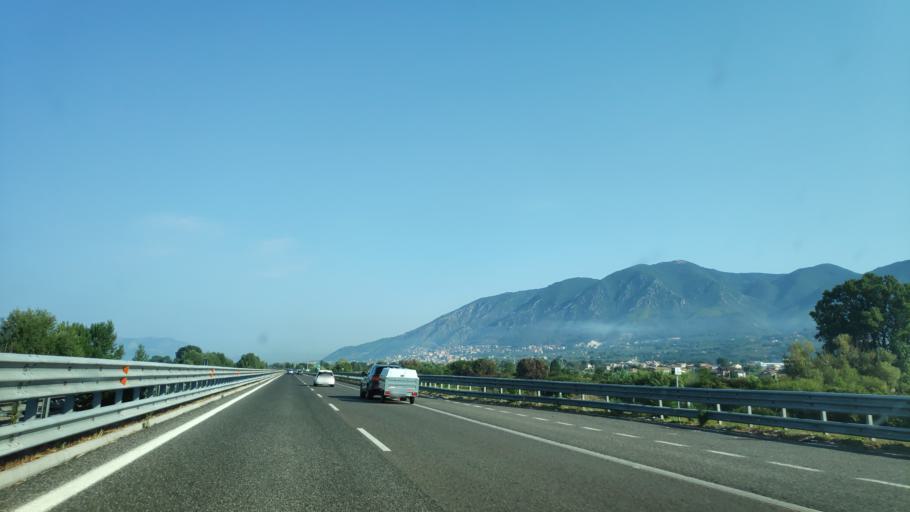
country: IT
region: Campania
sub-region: Provincia di Salerno
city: Sala Consilina
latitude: 40.3545
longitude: 15.6143
